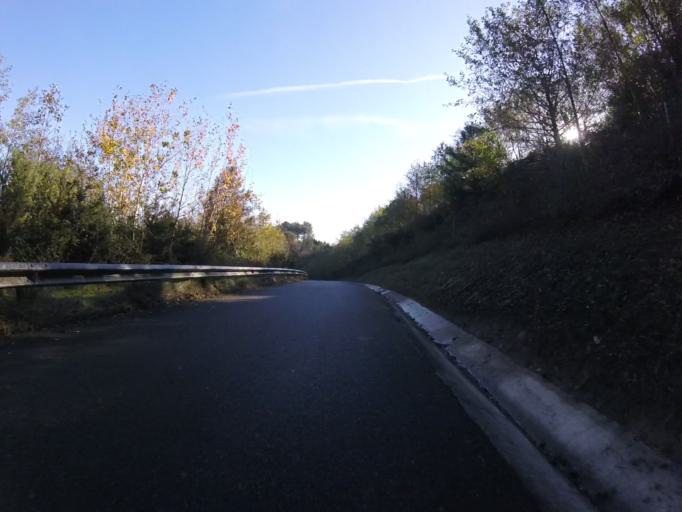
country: ES
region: Basque Country
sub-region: Provincia de Guipuzcoa
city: Usurbil
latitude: 43.2937
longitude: -2.0445
